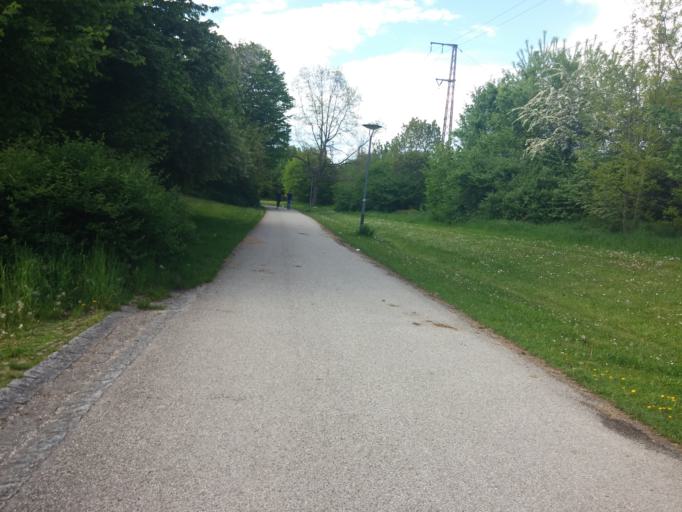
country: DE
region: Bavaria
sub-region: Upper Bavaria
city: Bogenhausen
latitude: 48.1447
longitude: 11.6495
